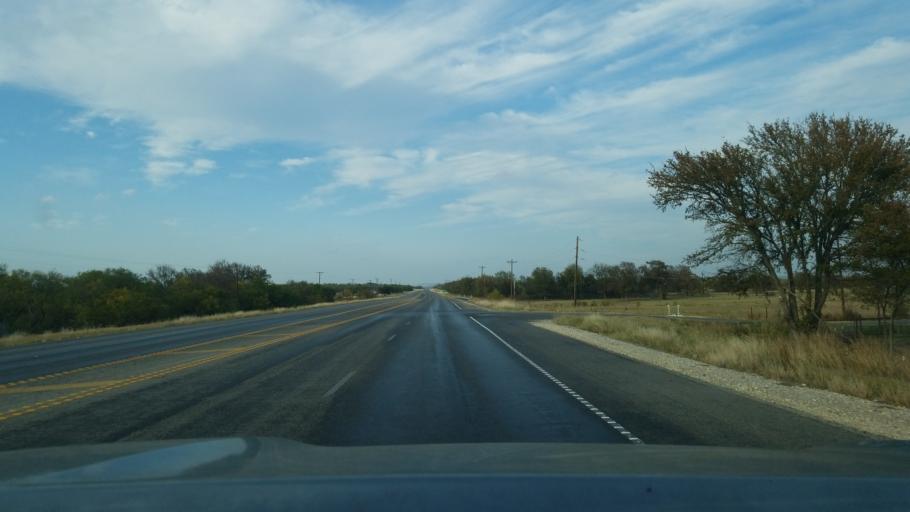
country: US
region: Texas
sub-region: Brown County
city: Early
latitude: 31.7836
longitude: -98.9469
